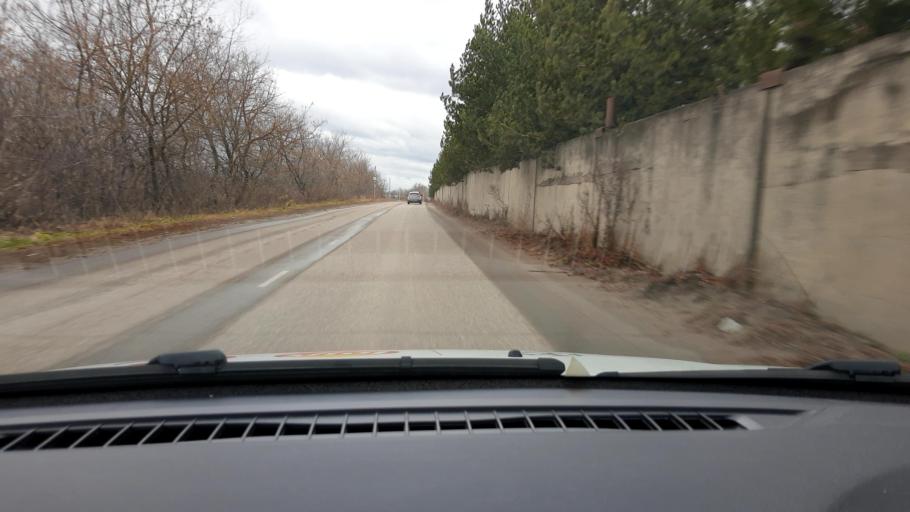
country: RU
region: Nizjnij Novgorod
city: Bogorodsk
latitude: 56.1158
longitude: 43.5332
